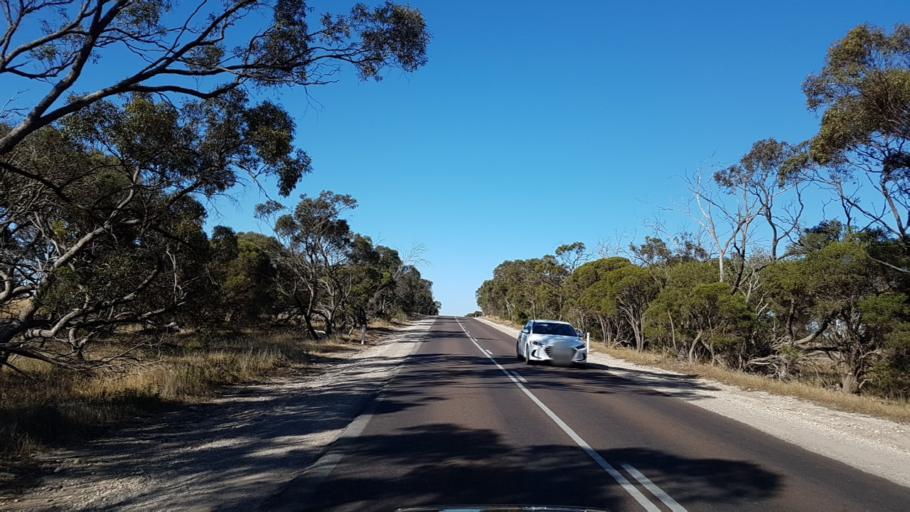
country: AU
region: South Australia
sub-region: Yorke Peninsula
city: Port Victoria
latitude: -34.7407
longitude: 137.6367
